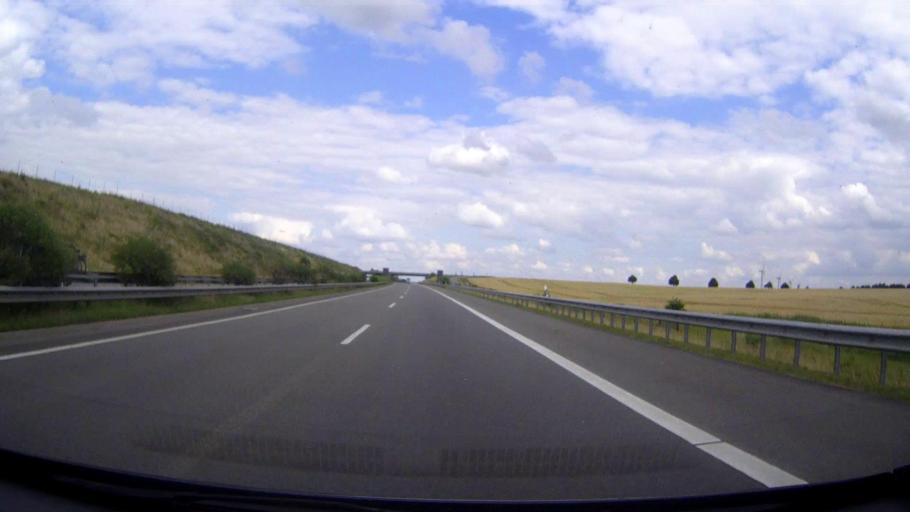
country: DE
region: Schleswig-Holstein
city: Weede
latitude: 53.9183
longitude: 10.3755
